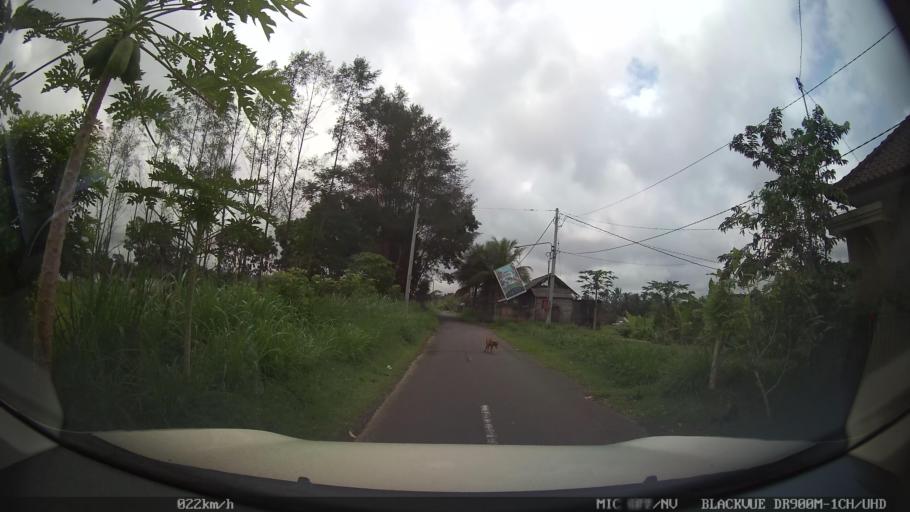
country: ID
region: Bali
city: Pemijian
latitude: -8.4378
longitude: 115.2269
